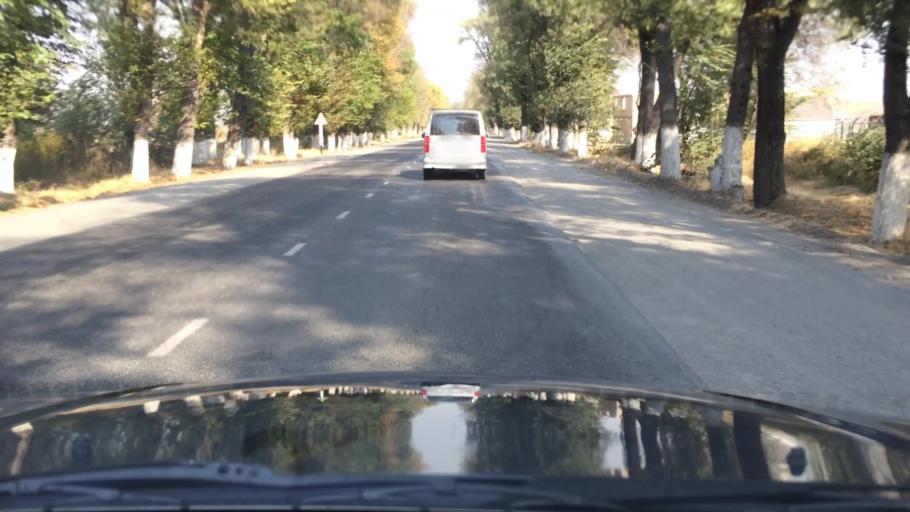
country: KG
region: Chuy
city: Lebedinovka
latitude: 42.9212
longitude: 74.6896
